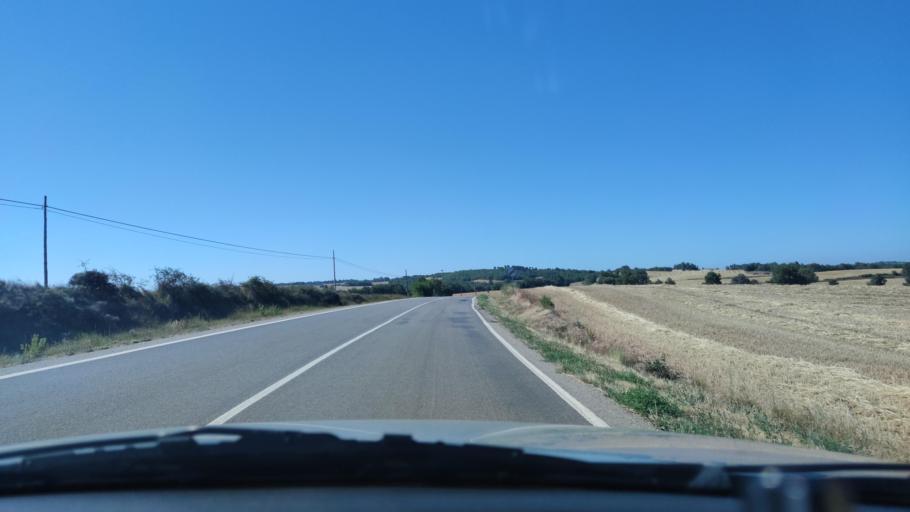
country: ES
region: Catalonia
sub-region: Provincia de Lleida
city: Solsona
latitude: 41.9377
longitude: 1.4972
